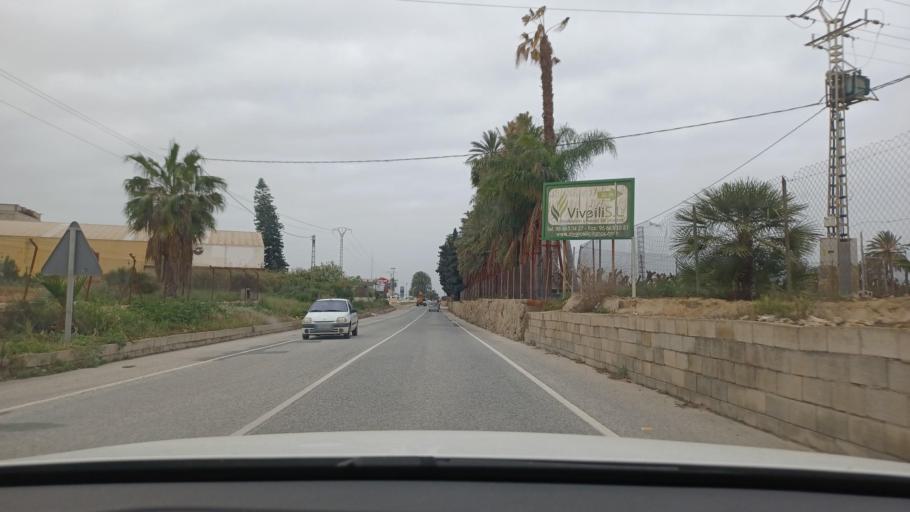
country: ES
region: Valencia
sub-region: Provincia de Alicante
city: Elche
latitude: 38.2434
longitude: -0.7074
